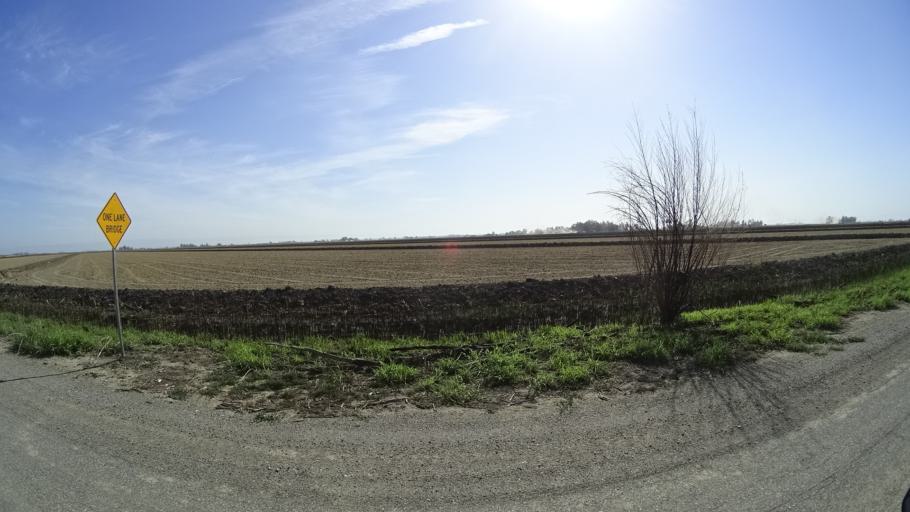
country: US
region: California
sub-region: Glenn County
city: Willows
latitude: 39.5853
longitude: -122.1168
